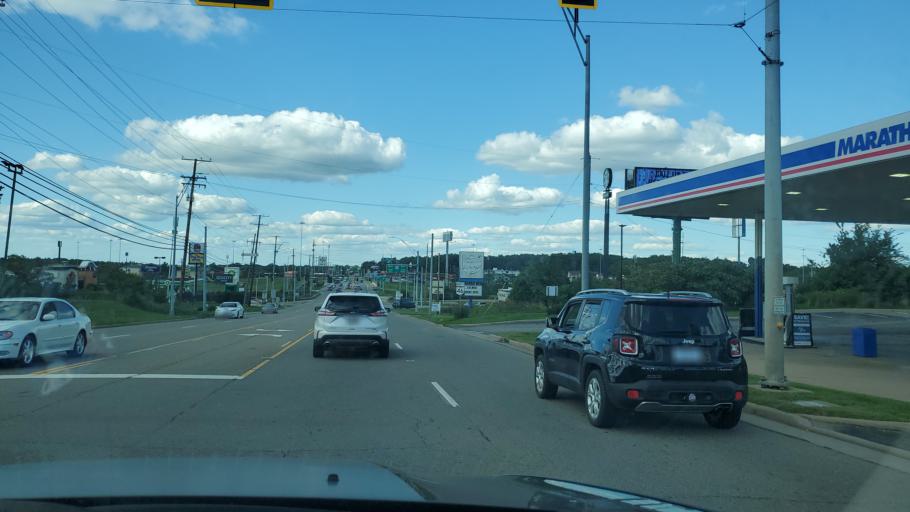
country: US
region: Ohio
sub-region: Mahoning County
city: Austintown
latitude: 41.1200
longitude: -80.7681
